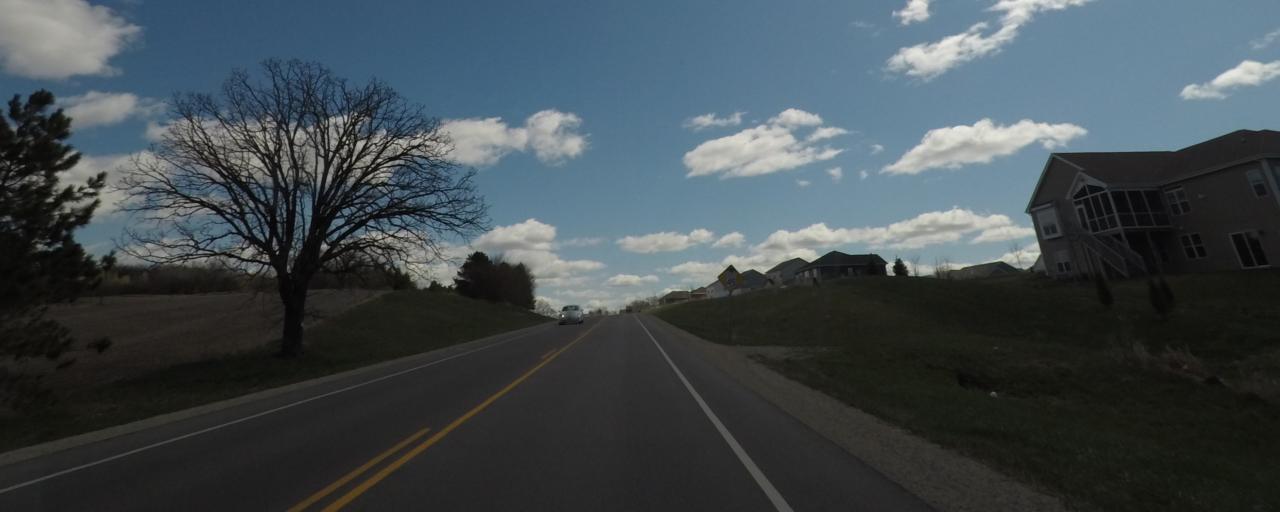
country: US
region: Wisconsin
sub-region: Jefferson County
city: Lake Mills
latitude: 43.0920
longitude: -88.9442
